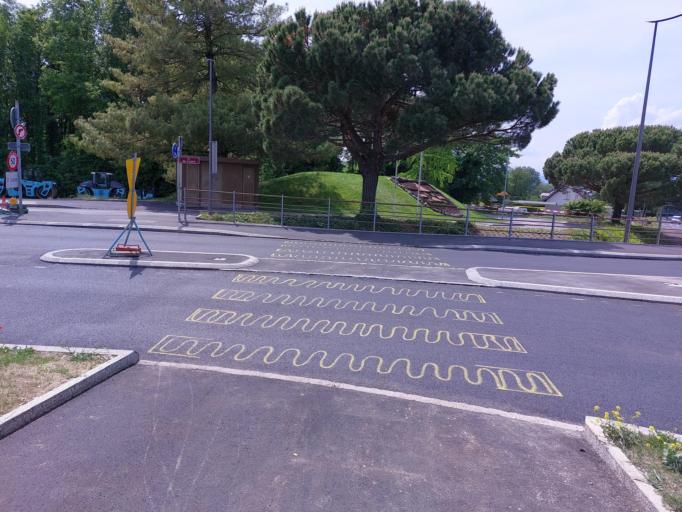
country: CH
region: Vaud
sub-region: Morges District
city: Preverenges
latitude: 46.5132
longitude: 6.5459
